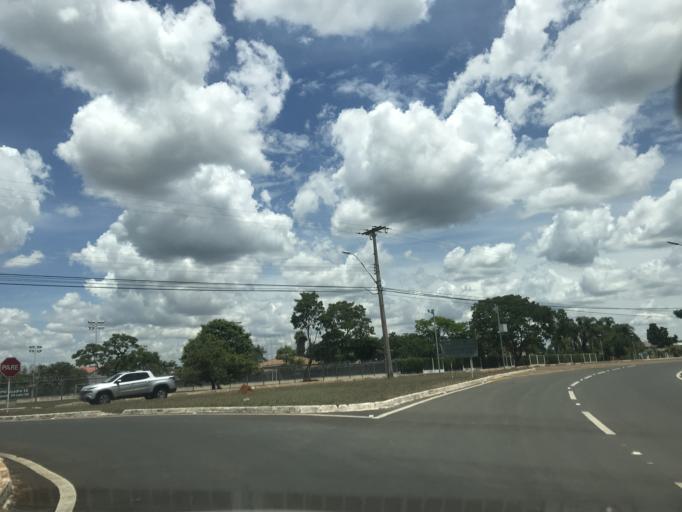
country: BR
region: Federal District
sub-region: Brasilia
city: Brasilia
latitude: -15.9093
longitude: -47.9467
